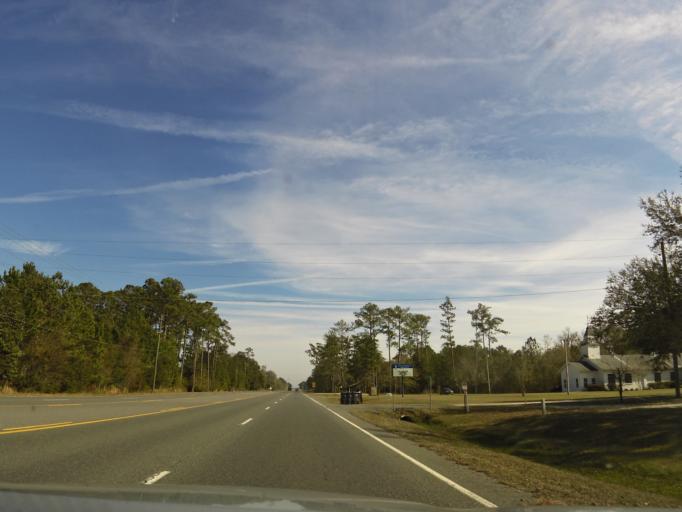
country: US
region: Georgia
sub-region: Brantley County
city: Nahunta
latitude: 31.2296
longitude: -81.7854
